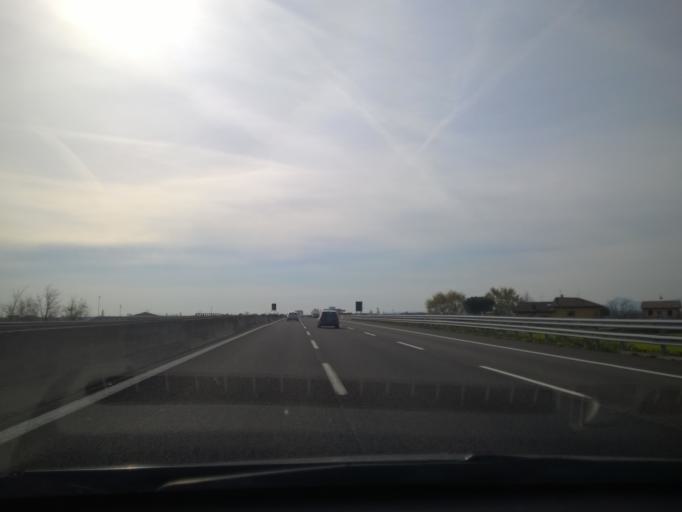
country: IT
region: Emilia-Romagna
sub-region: Forli-Cesena
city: Gatteo-Sant'Angelo
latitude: 44.1290
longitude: 12.3771
